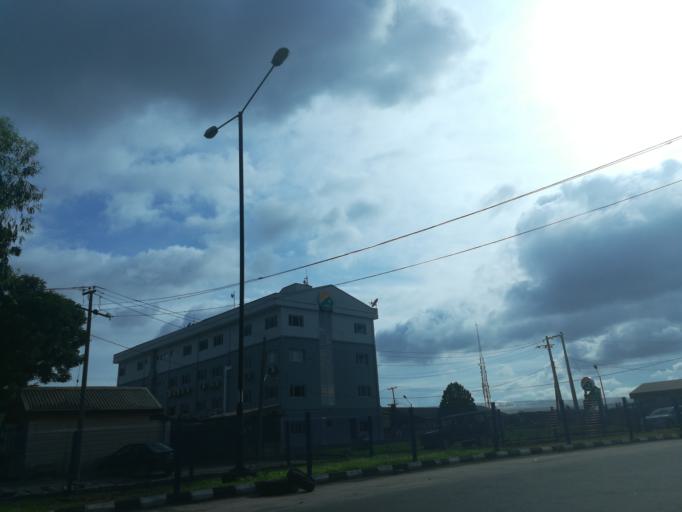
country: NG
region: Lagos
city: Ikeja
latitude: 6.6204
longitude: 3.3564
